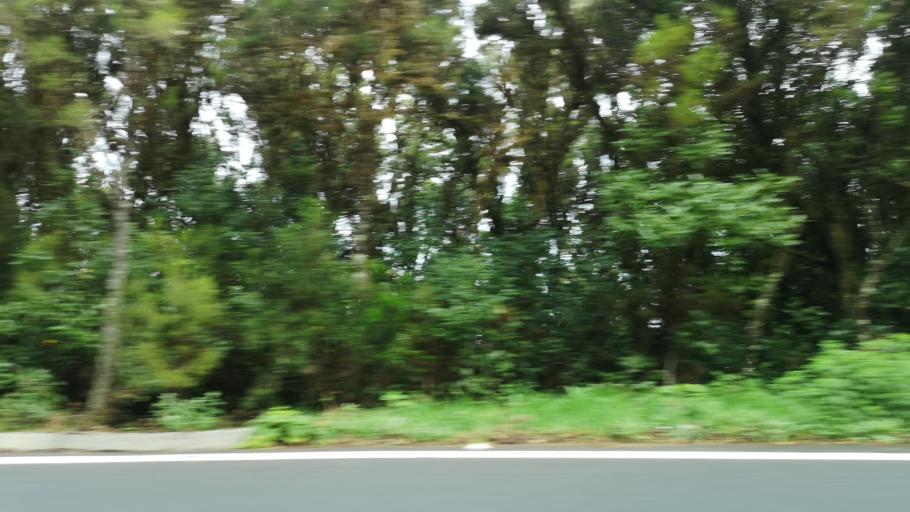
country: ES
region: Canary Islands
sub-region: Provincia de Santa Cruz de Tenerife
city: Vallehermosa
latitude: 28.1412
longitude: -17.2838
